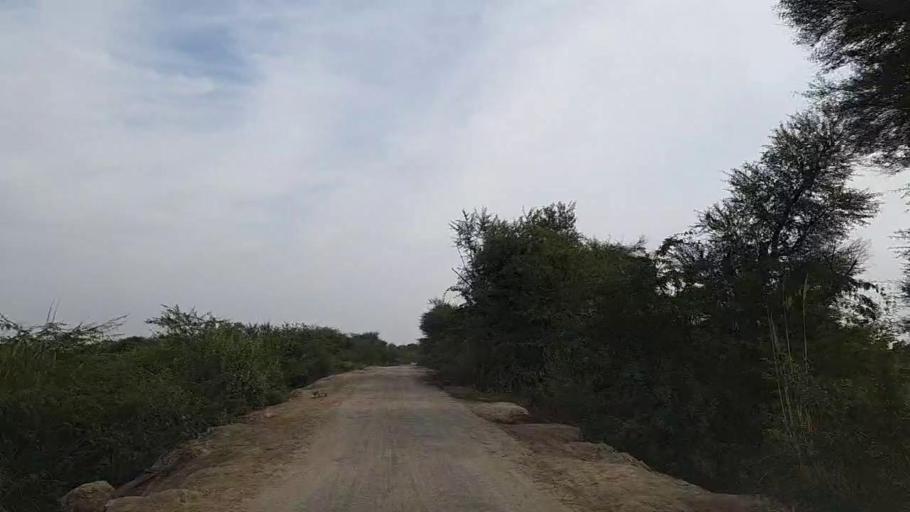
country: PK
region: Sindh
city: Jam Sahib
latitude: 26.4380
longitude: 68.6284
